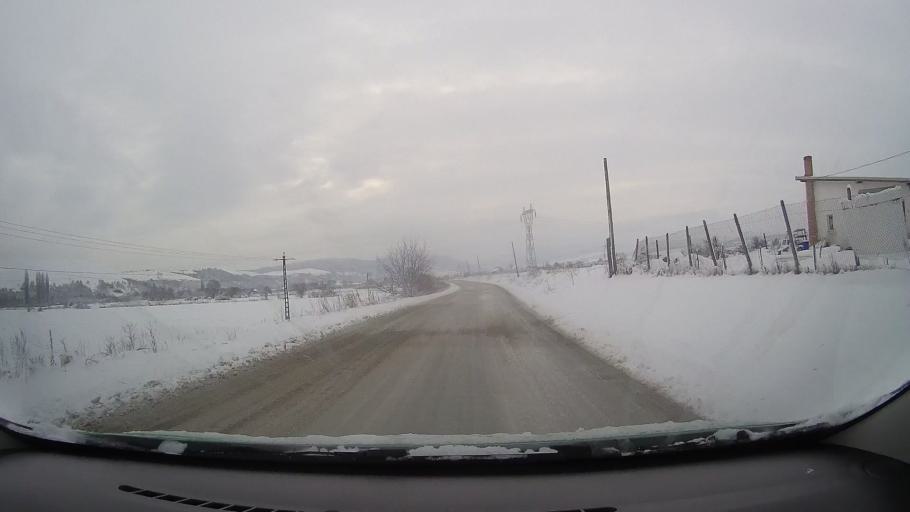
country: RO
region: Alba
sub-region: Comuna Pianu
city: Pianu de Jos
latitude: 45.9535
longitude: 23.4779
